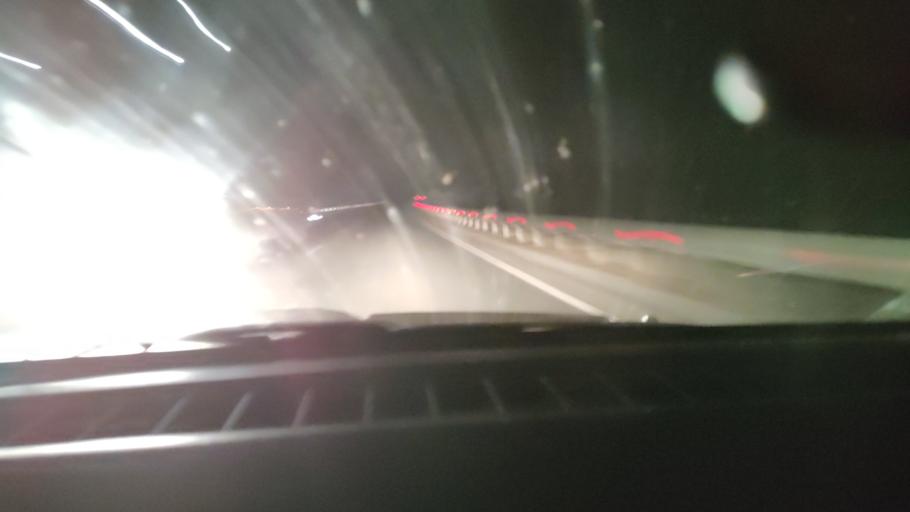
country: RU
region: Saratov
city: Khvalynsk
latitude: 52.4508
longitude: 48.0121
